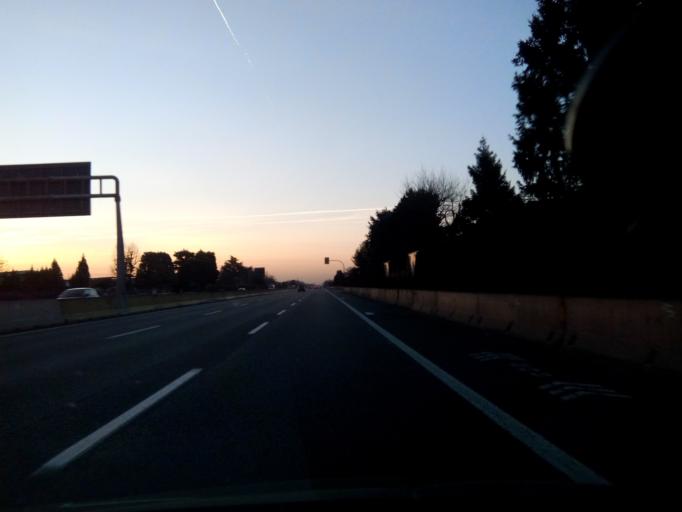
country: IT
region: Lombardy
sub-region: Citta metropolitana di Milano
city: Cerro Maggiore
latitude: 45.6006
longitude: 8.9508
